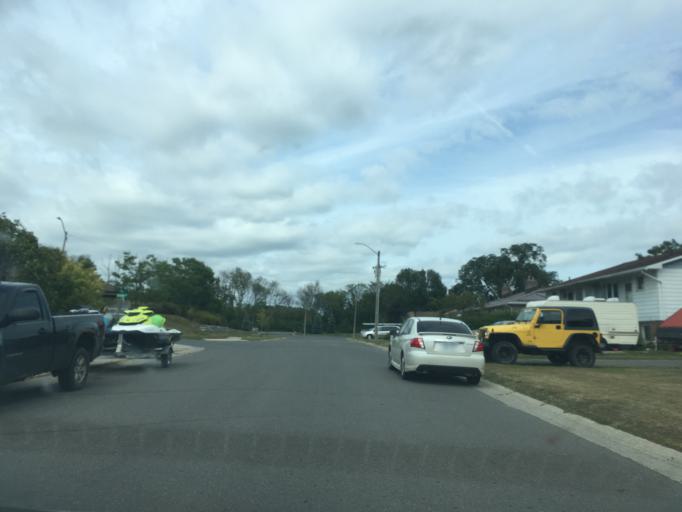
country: CA
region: Ontario
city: Kingston
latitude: 44.2743
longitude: -76.4778
